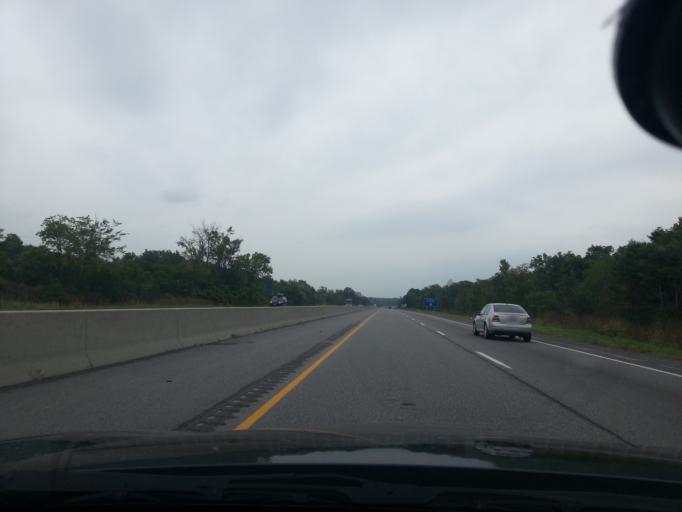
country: CA
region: Ontario
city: Gananoque
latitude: 44.3345
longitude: -76.2208
